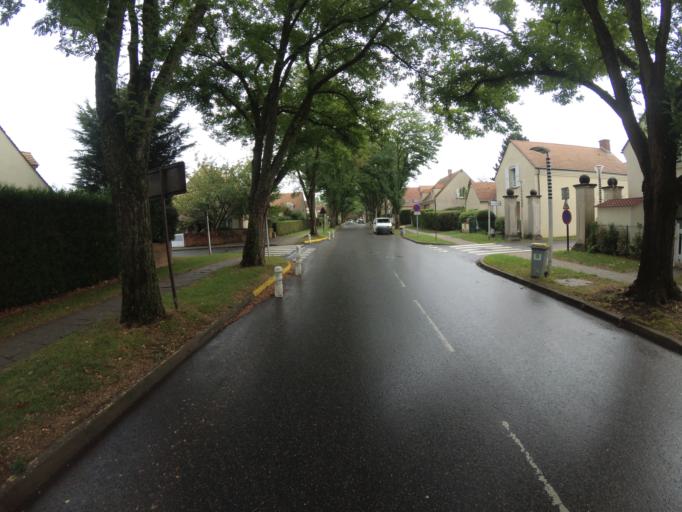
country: FR
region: Ile-de-France
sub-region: Departement de Seine-et-Marne
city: Bussy-Saint-Georges
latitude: 48.8424
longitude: 2.7064
